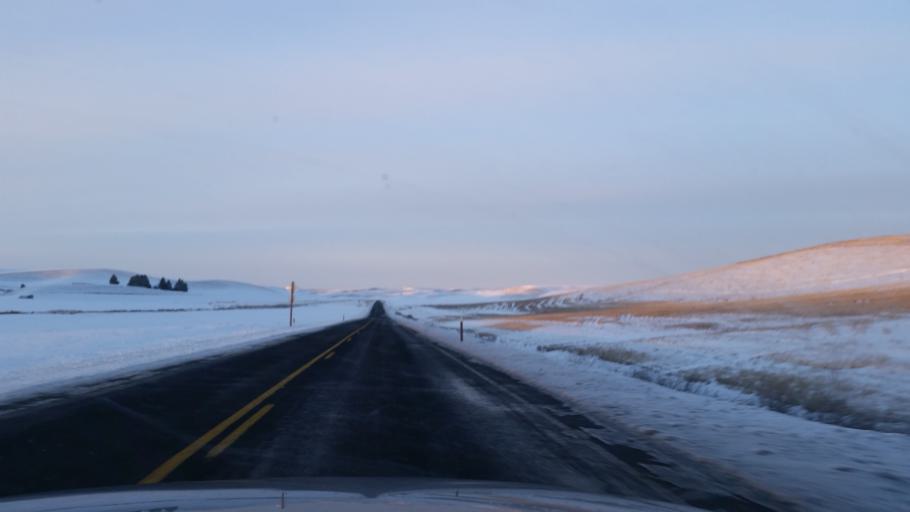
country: US
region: Washington
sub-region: Spokane County
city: Cheney
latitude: 47.1593
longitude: -117.8712
